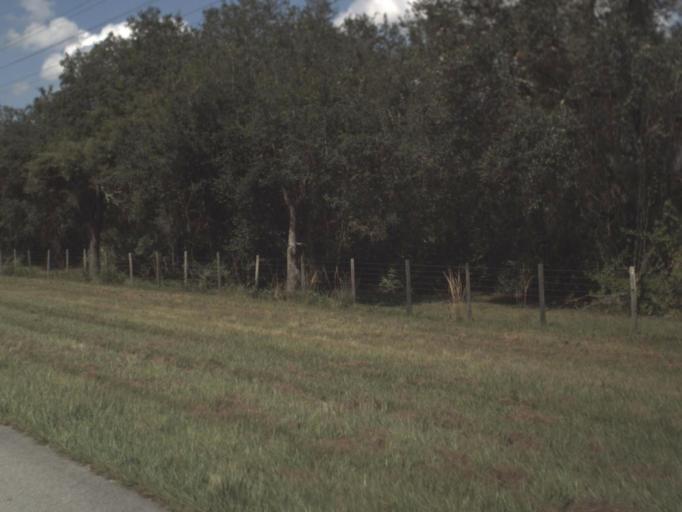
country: US
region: Florida
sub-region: Okeechobee County
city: Okeechobee
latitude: 27.3878
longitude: -81.0183
